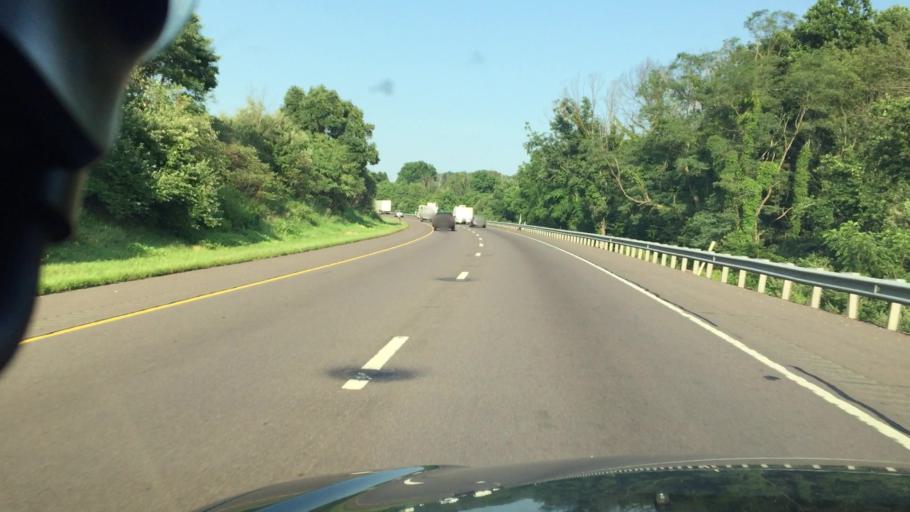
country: US
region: Pennsylvania
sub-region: Columbia County
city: Mifflinville
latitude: 41.0103
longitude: -76.2924
